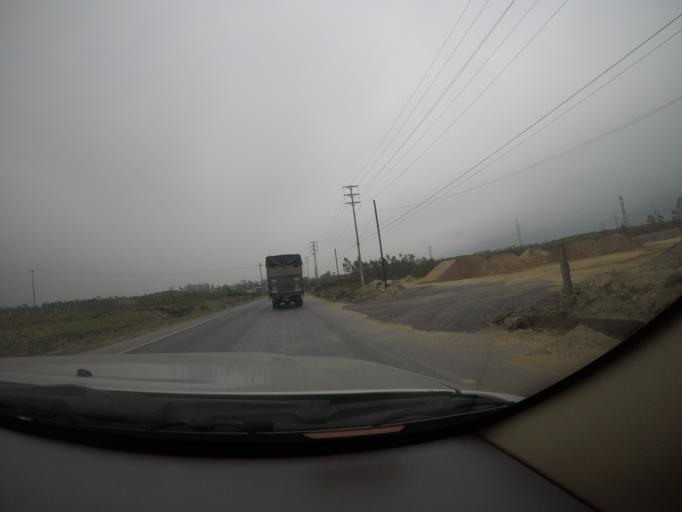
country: VN
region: Ha Tinh
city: Ky Anh
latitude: 18.0177
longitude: 106.3894
